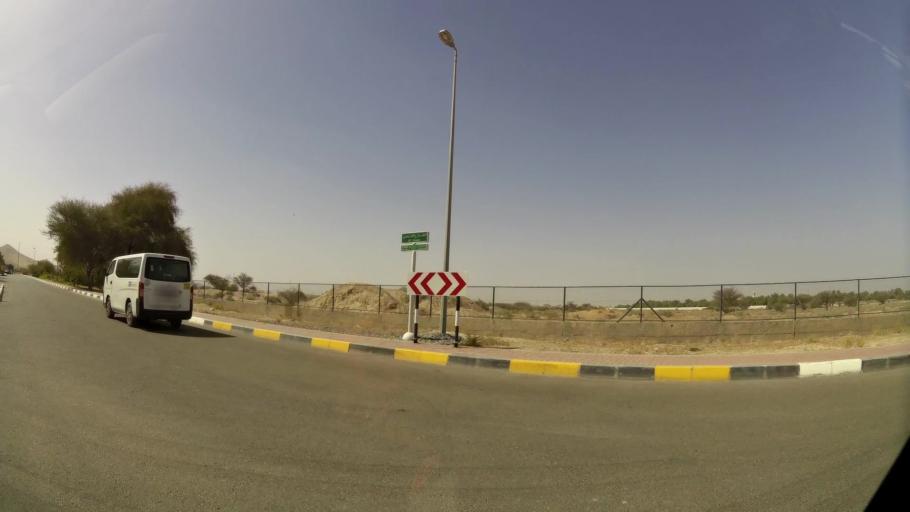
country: OM
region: Al Buraimi
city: Al Buraymi
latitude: 24.2981
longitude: 55.7981
